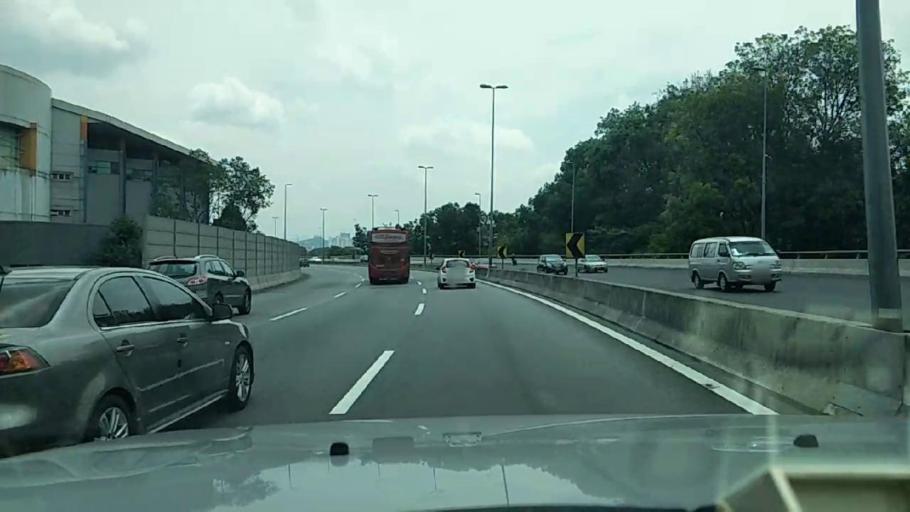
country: MY
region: Selangor
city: Kampong Baharu Balakong
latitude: 3.0590
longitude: 101.6882
